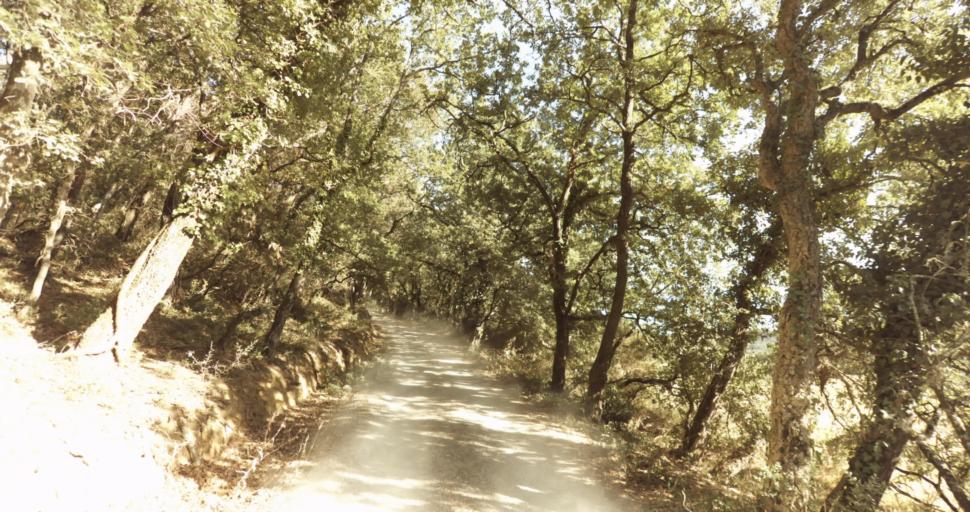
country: FR
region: Provence-Alpes-Cote d'Azur
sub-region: Departement du Var
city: Gassin
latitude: 43.2244
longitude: 6.5803
